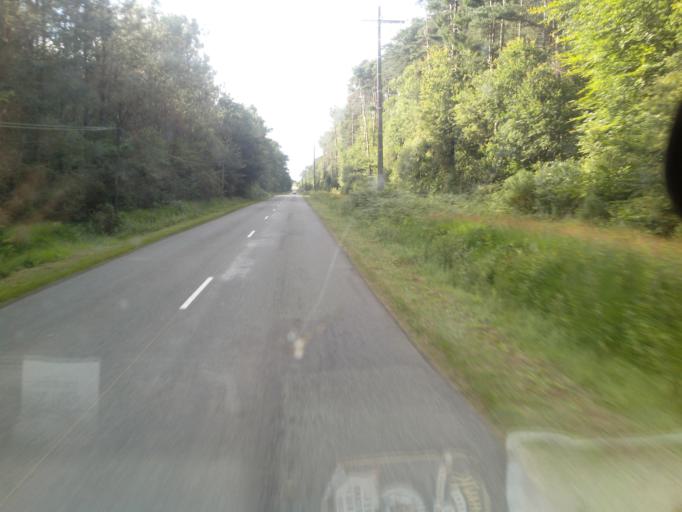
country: FR
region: Brittany
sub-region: Departement d'Ille-et-Vilaine
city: Paimpont
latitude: 48.0284
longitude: -2.1751
